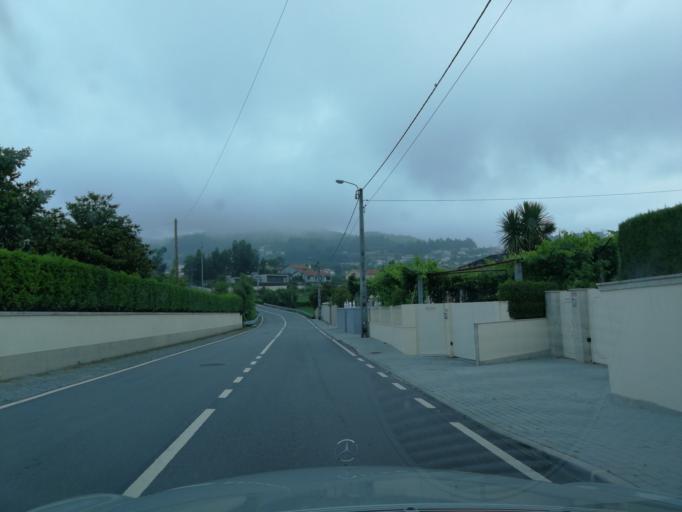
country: PT
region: Braga
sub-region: Guimaraes
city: Ponte
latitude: 41.5095
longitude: -8.3539
